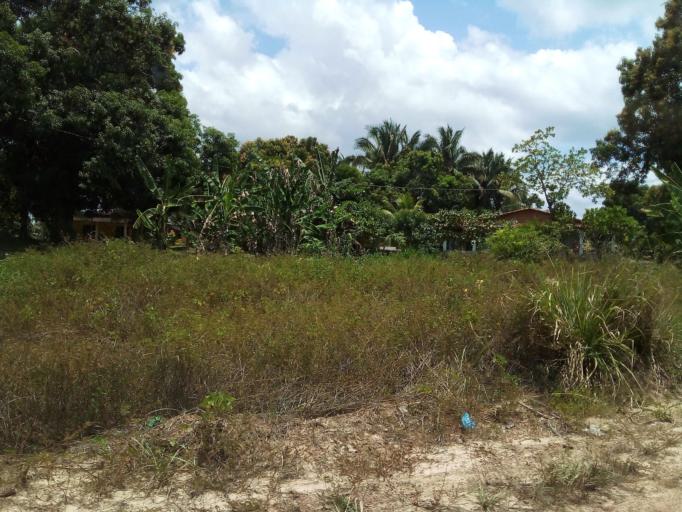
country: BR
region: Maranhao
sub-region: Itapecuru Mirim
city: Itapecuru Mirim
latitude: -3.0552
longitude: -44.3422
